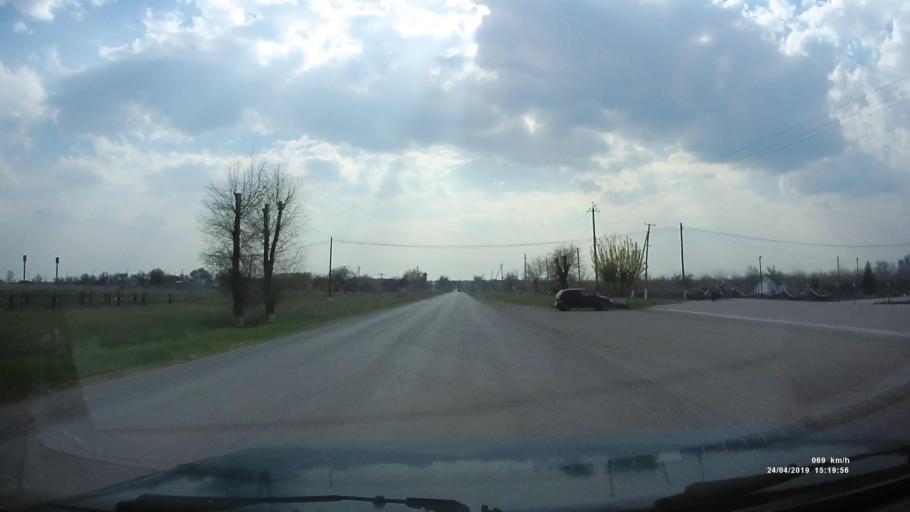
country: RU
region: Rostov
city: Remontnoye
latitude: 46.5375
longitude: 43.1395
